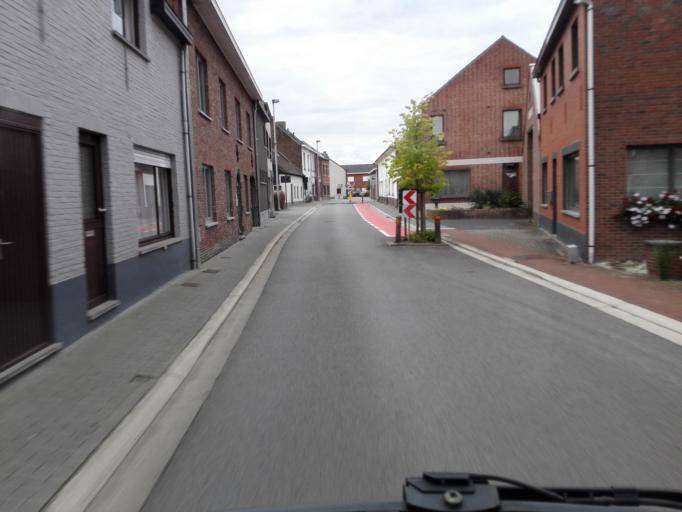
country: BE
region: Flanders
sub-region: Provincie Vlaams-Brabant
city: Boortmeerbeek
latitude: 50.9915
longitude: 4.5562
